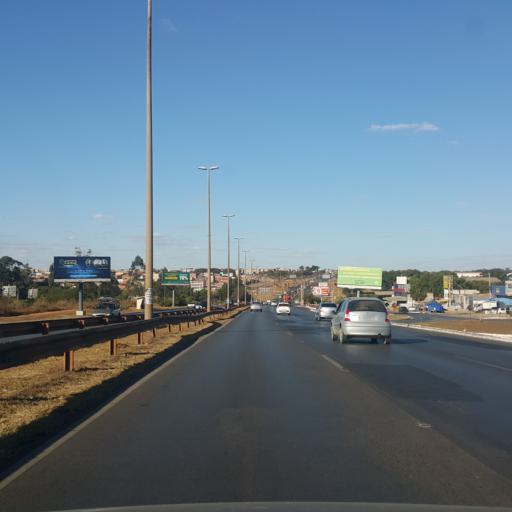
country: BR
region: Federal District
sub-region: Brasilia
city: Brasilia
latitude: -15.7869
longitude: -48.0083
